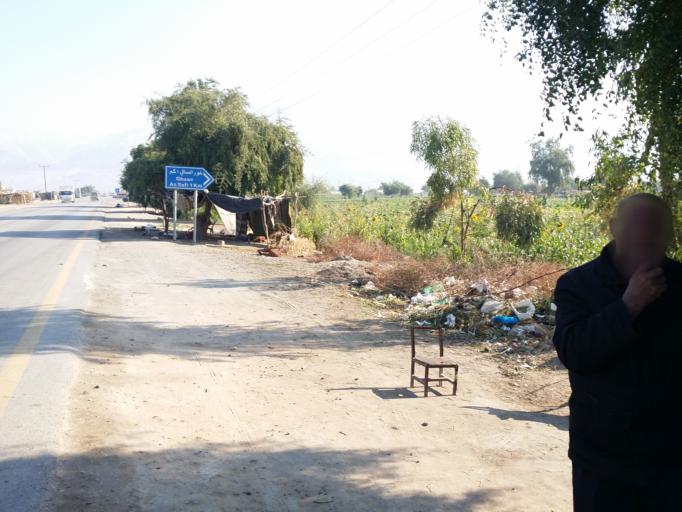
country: JO
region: Karak
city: Safi
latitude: 31.0529
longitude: 35.4736
